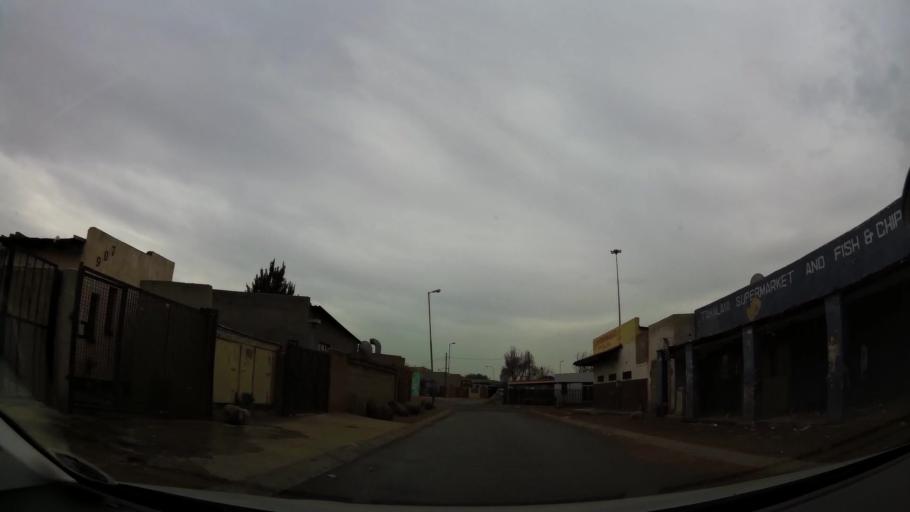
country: ZA
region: Gauteng
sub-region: City of Johannesburg Metropolitan Municipality
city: Soweto
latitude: -26.2515
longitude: 27.8766
